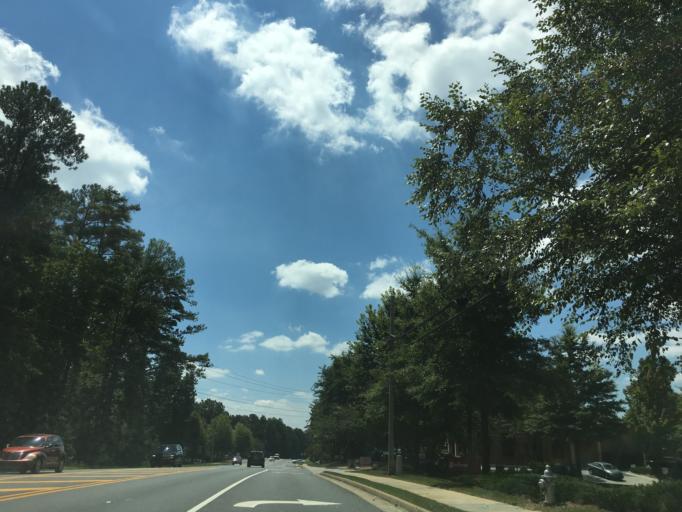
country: US
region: Georgia
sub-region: Fulton County
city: Milton
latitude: 34.1165
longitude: -84.2697
